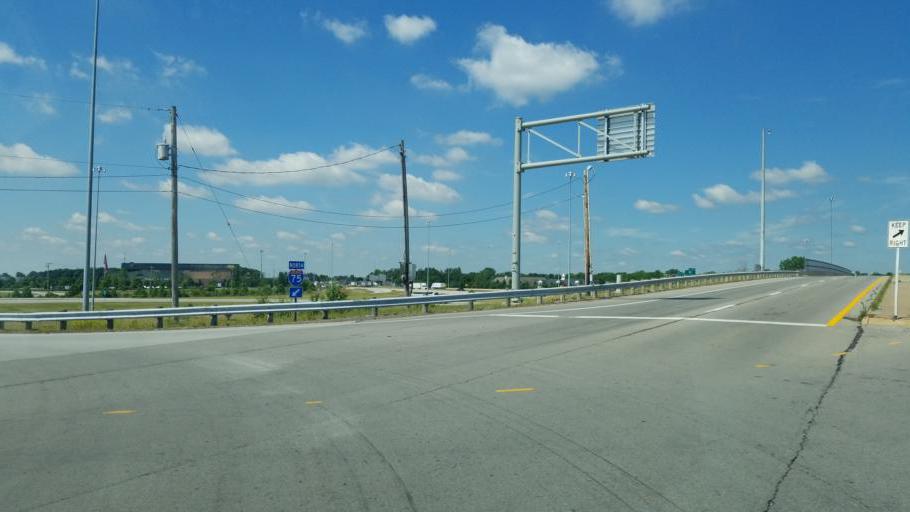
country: US
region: Ohio
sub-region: Wood County
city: Perrysburg
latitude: 41.5650
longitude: -83.5839
